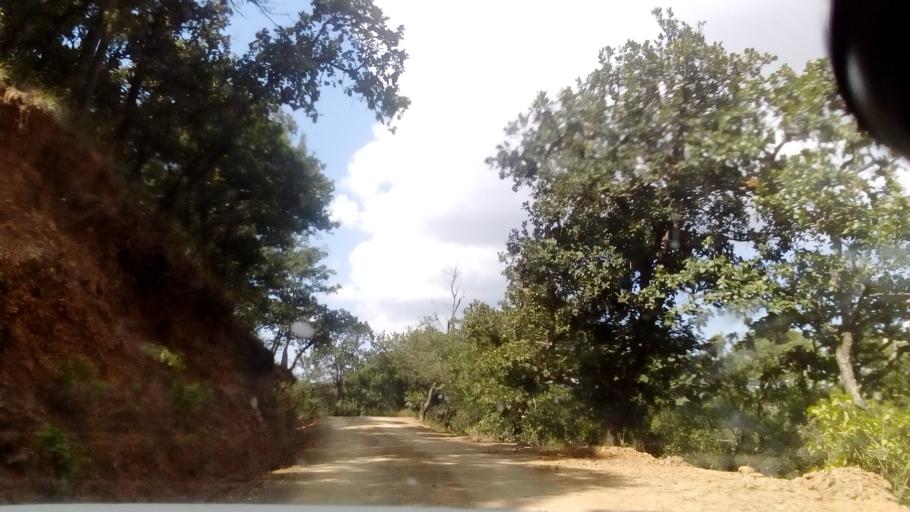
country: MX
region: Guanajuato
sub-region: Silao de la Victoria
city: San Francisco (Banos de Agua Caliente)
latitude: 21.1686
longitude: -101.4586
